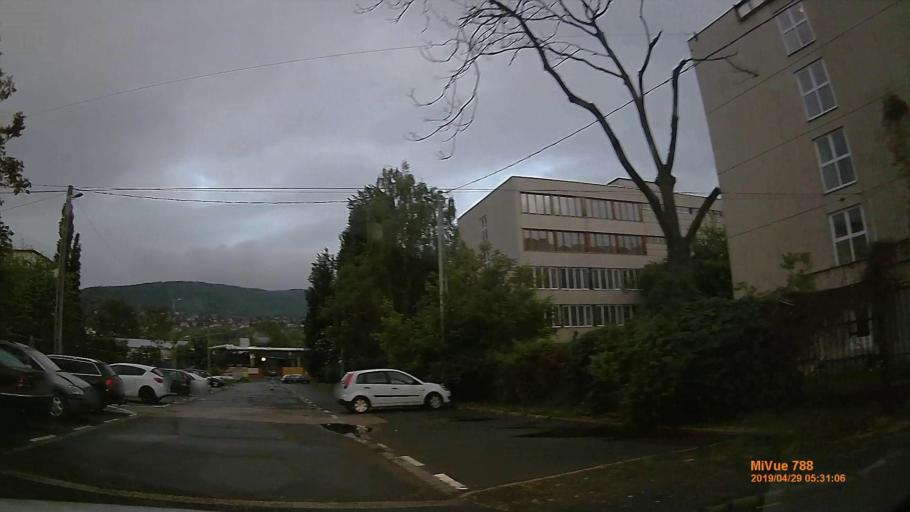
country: HU
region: Budapest
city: Budapest III. keruelet
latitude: 47.5524
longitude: 19.0352
